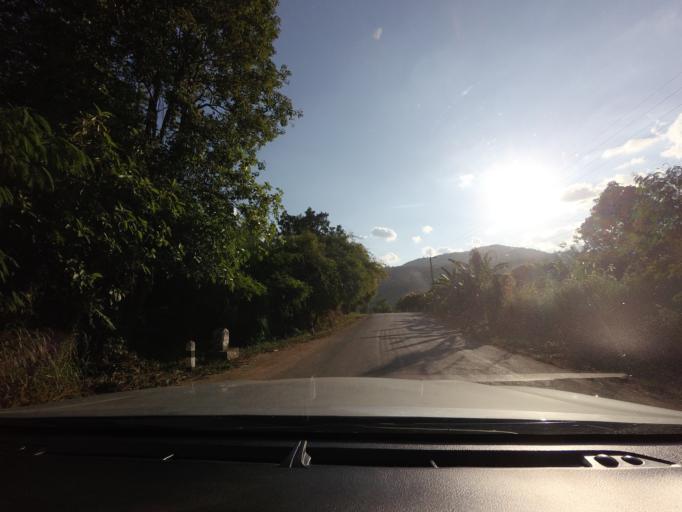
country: TH
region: Chiang Mai
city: Chai Prakan
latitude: 19.6163
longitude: 99.1635
